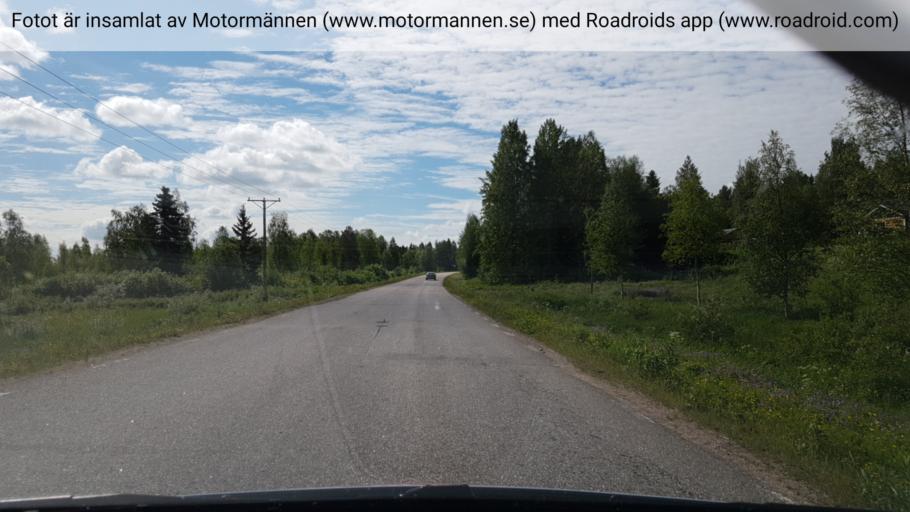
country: FI
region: Lapland
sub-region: Torniolaakso
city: Pello
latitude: 66.6429
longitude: 23.8645
